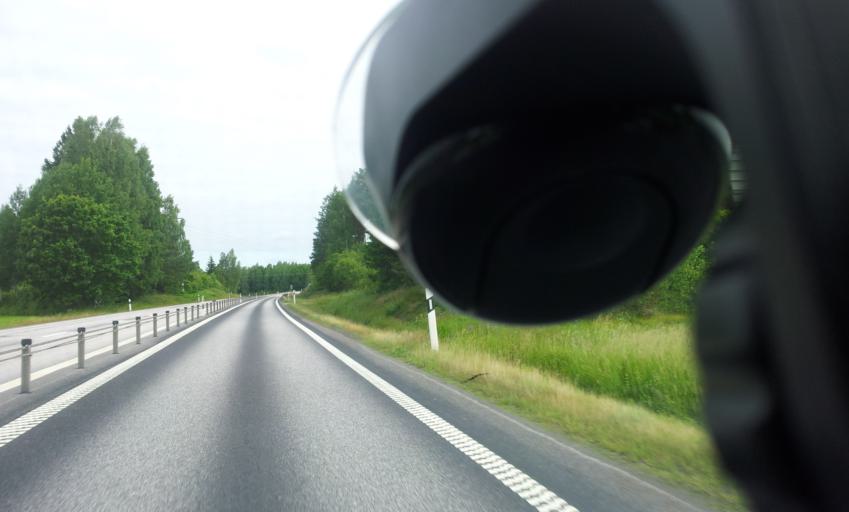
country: SE
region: Kalmar
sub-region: Vasterviks Kommun
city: Forserum
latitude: 58.0692
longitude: 16.5210
